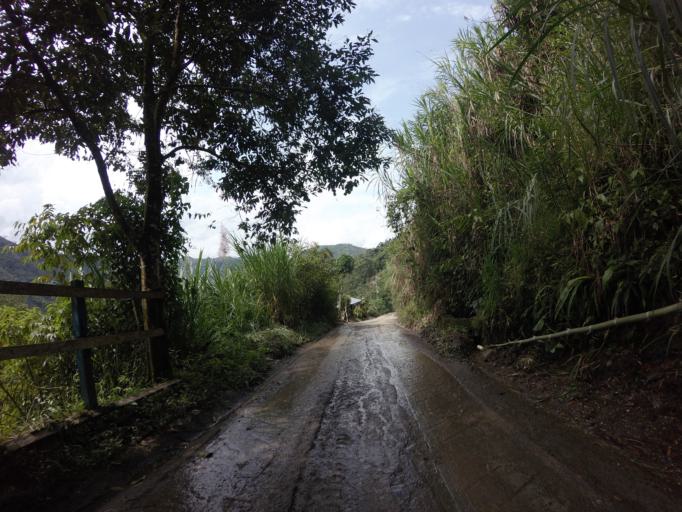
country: CO
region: Caldas
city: Marquetalia
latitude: 5.3228
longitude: -75.0446
